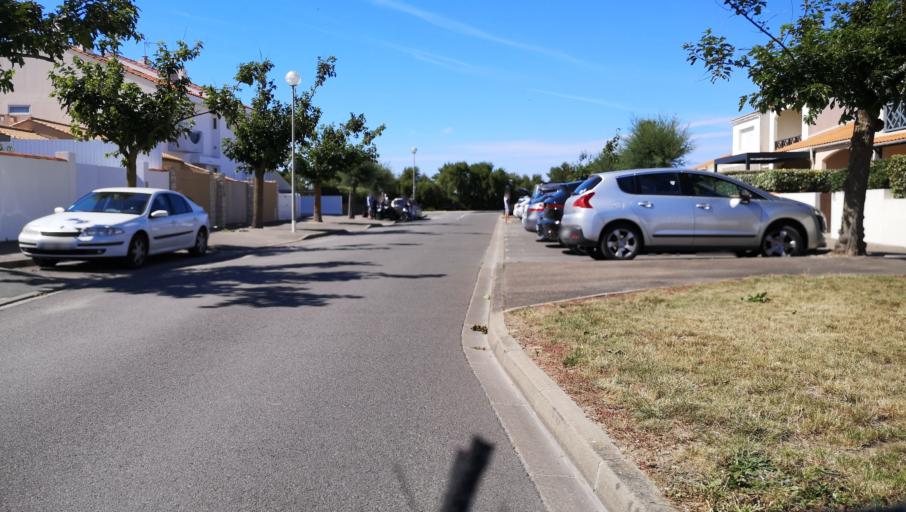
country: FR
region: Pays de la Loire
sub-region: Departement de la Vendee
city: Les Sables-d'Olonne
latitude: 46.4962
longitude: -1.8131
